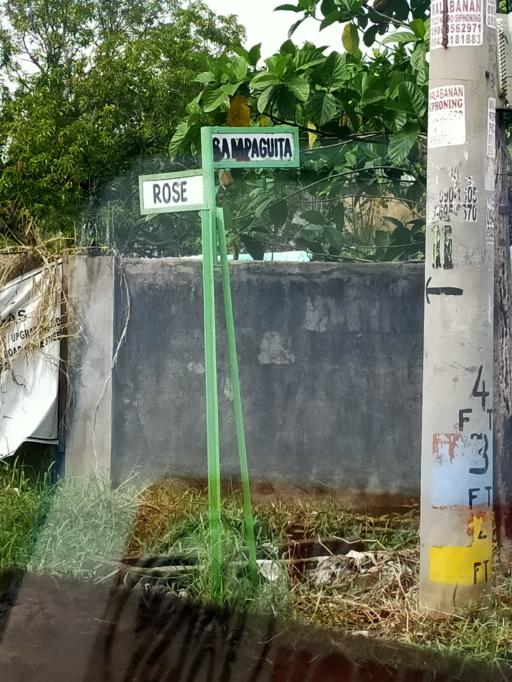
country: PH
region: Central Luzon
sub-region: Province of Pampanga
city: Pau
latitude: 15.0118
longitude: 120.7111
